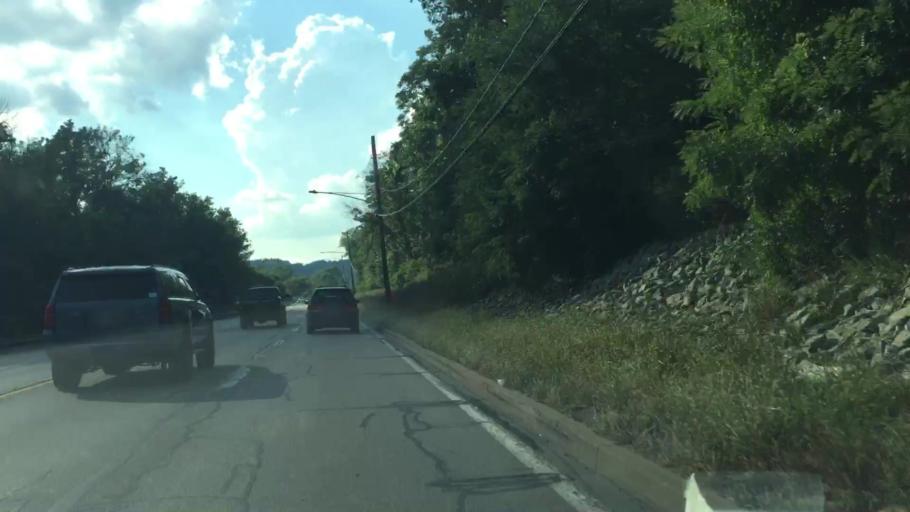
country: US
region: Pennsylvania
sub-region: Allegheny County
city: Coraopolis
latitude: 40.5283
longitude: -80.1597
